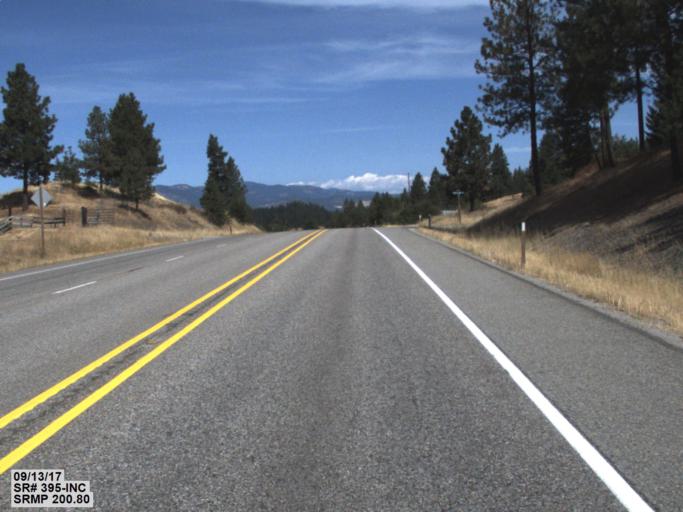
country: US
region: Washington
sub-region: Stevens County
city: Chewelah
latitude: 48.1875
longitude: -117.7004
